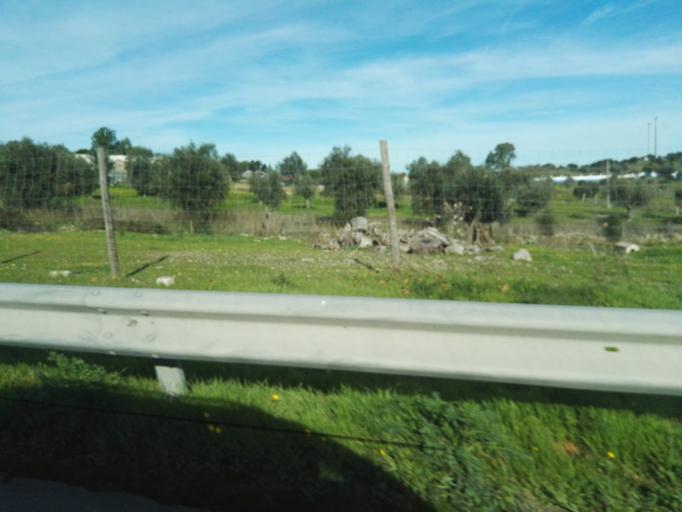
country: PT
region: Evora
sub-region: Mora
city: Mora
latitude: 38.8925
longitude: -8.0169
